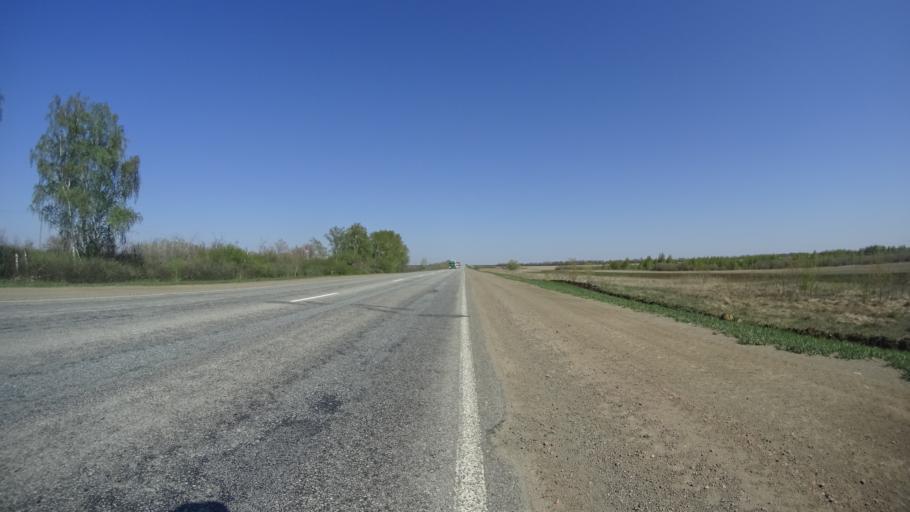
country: RU
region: Chelyabinsk
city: Troitsk
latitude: 54.1999
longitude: 61.4323
